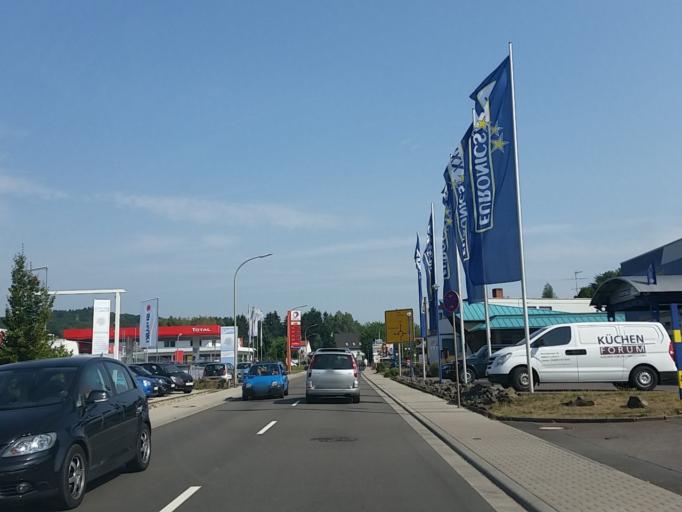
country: DE
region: Saarland
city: Lebach
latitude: 49.4117
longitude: 6.8945
